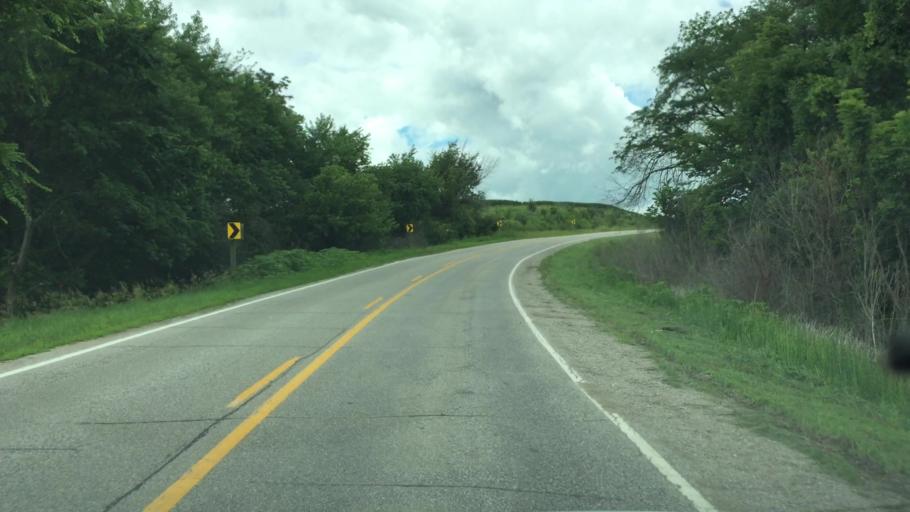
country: US
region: Iowa
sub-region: Jasper County
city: Monroe
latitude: 41.5737
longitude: -93.0398
